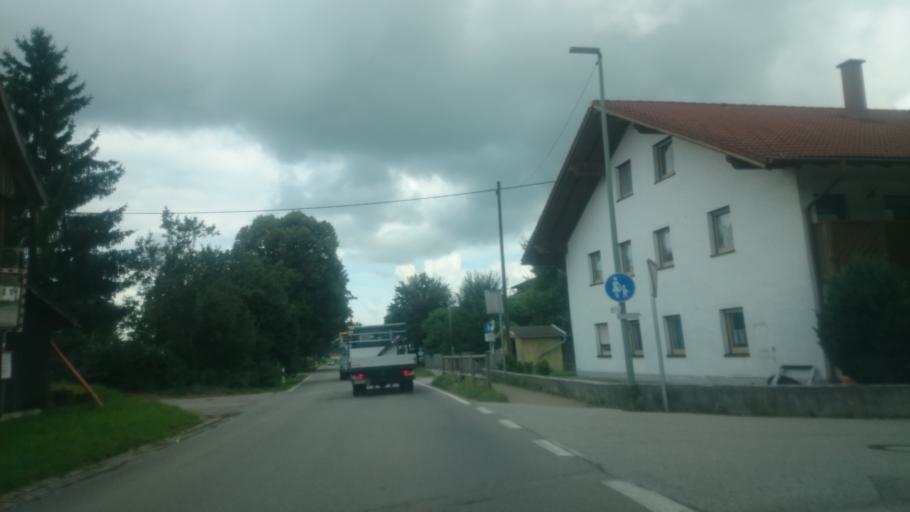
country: DE
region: Bavaria
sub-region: Swabia
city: Gunzach
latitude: 47.8120
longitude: 10.4456
